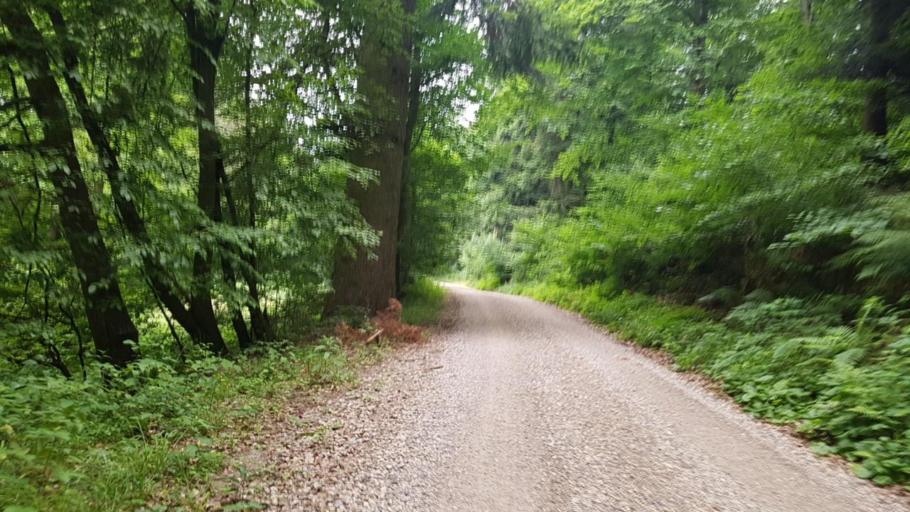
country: DE
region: North Rhine-Westphalia
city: Stolberg
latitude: 50.7423
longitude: 6.2840
